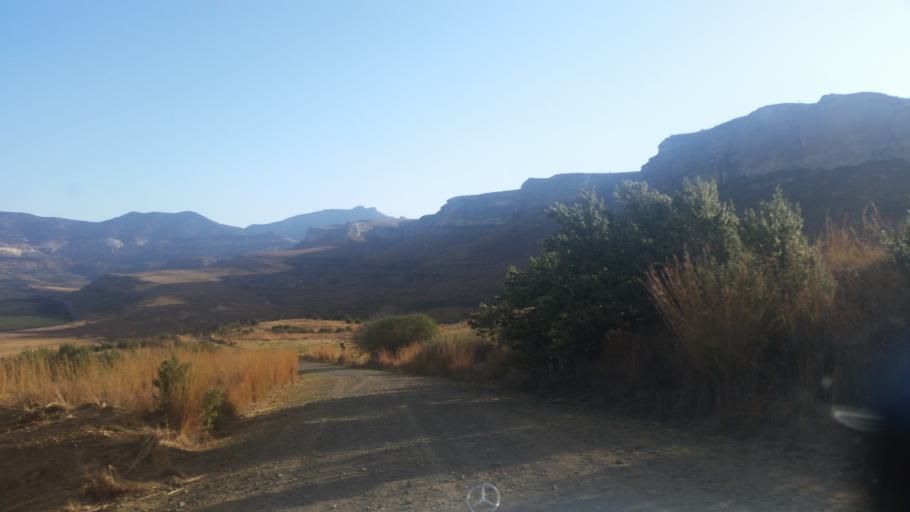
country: ZA
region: Orange Free State
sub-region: Thabo Mofutsanyana District Municipality
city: Phuthaditjhaba
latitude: -28.4938
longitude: 28.6894
